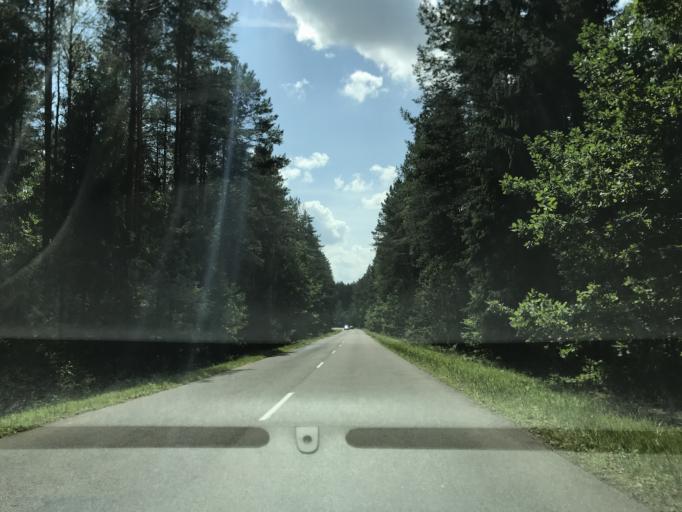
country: BY
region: Minsk
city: Rakaw
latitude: 53.9889
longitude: 26.9906
